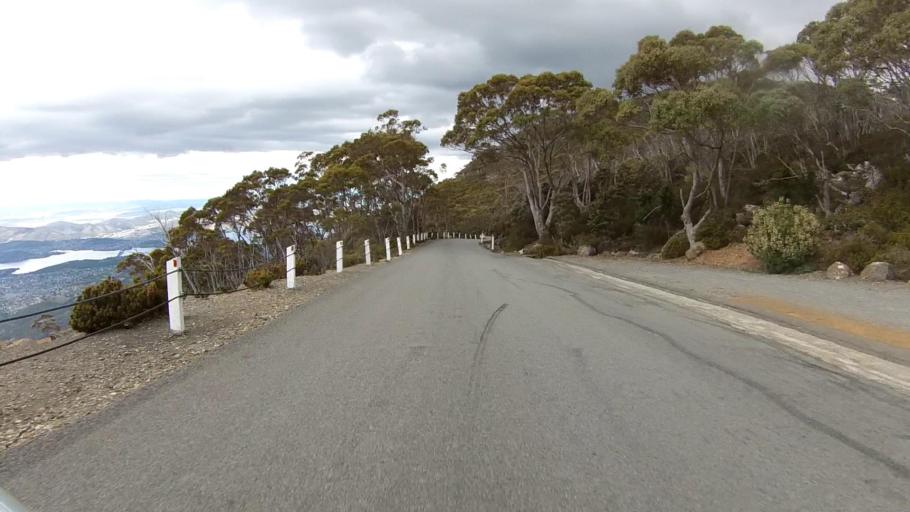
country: AU
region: Tasmania
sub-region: Glenorchy
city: West Moonah
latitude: -42.8872
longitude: 147.2237
